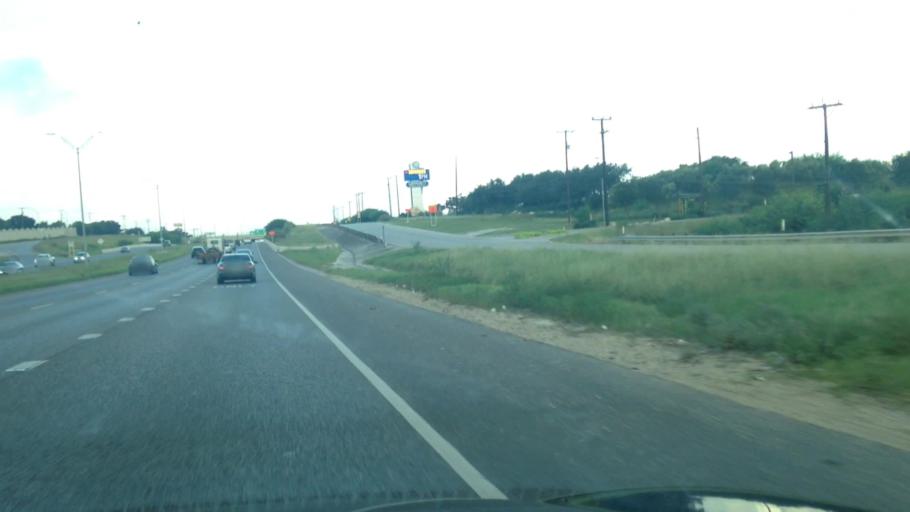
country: US
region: Texas
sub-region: Bexar County
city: Hollywood Park
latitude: 29.6046
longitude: -98.4511
